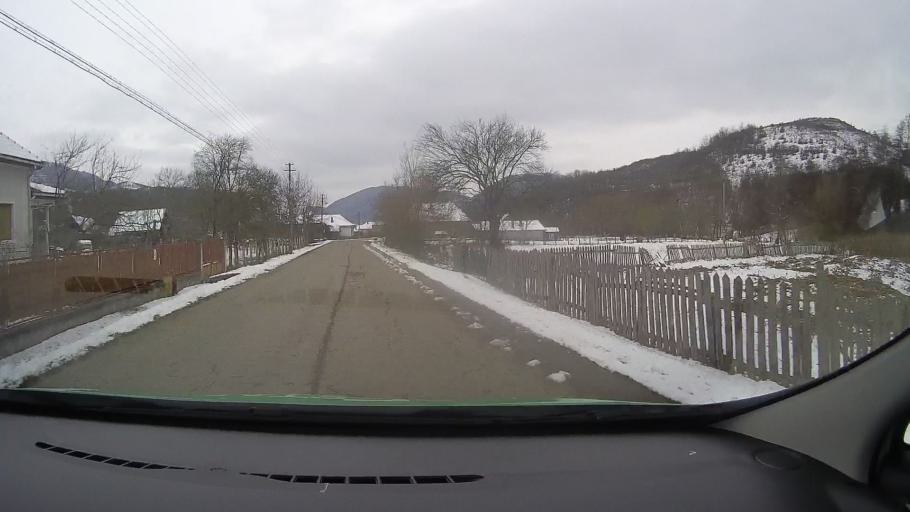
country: RO
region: Hunedoara
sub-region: Comuna Balsa
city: Balsa
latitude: 46.0310
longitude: 23.0890
